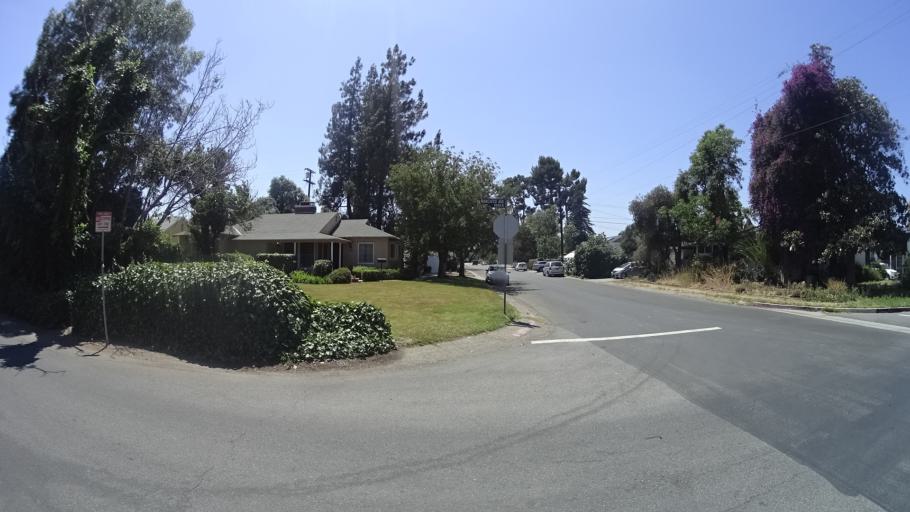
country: US
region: California
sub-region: Los Angeles County
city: Van Nuys
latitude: 34.1902
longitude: -118.4356
